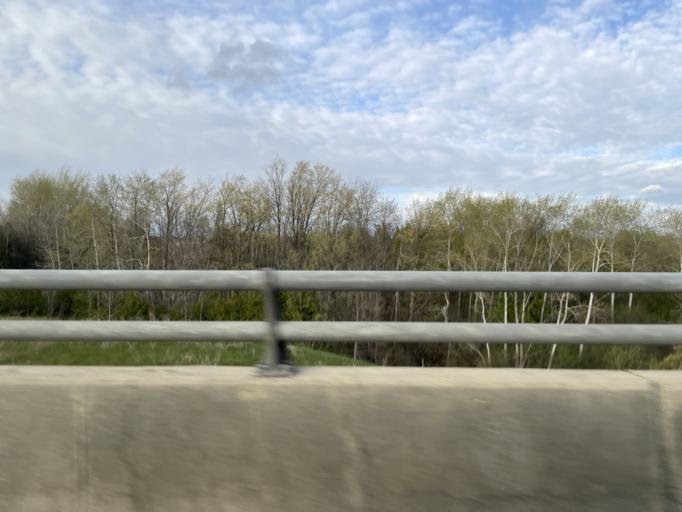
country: CA
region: Ontario
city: Waterloo
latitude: 43.4835
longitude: -80.4116
